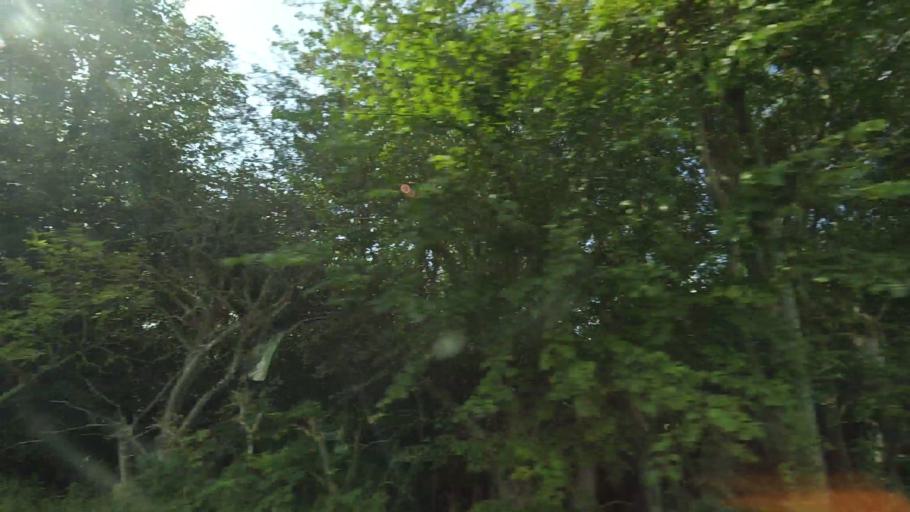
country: DK
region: Central Jutland
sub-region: Syddjurs Kommune
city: Ryomgard
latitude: 56.4664
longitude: 10.5172
